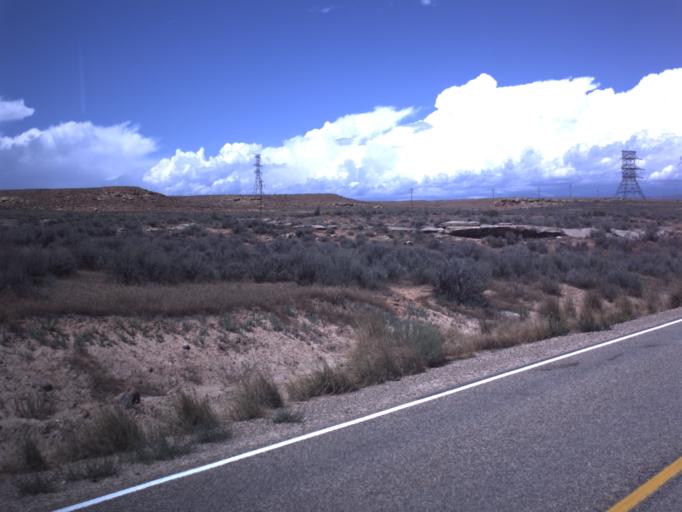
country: US
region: Utah
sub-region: Uintah County
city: Maeser
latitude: 40.2678
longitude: -109.6837
